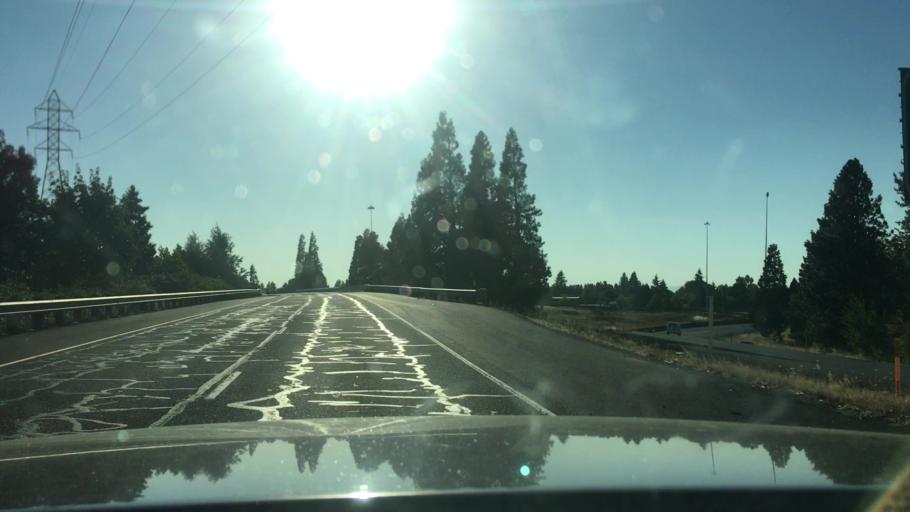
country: US
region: Oregon
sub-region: Lane County
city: Springfield
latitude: 44.0635
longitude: -123.0447
